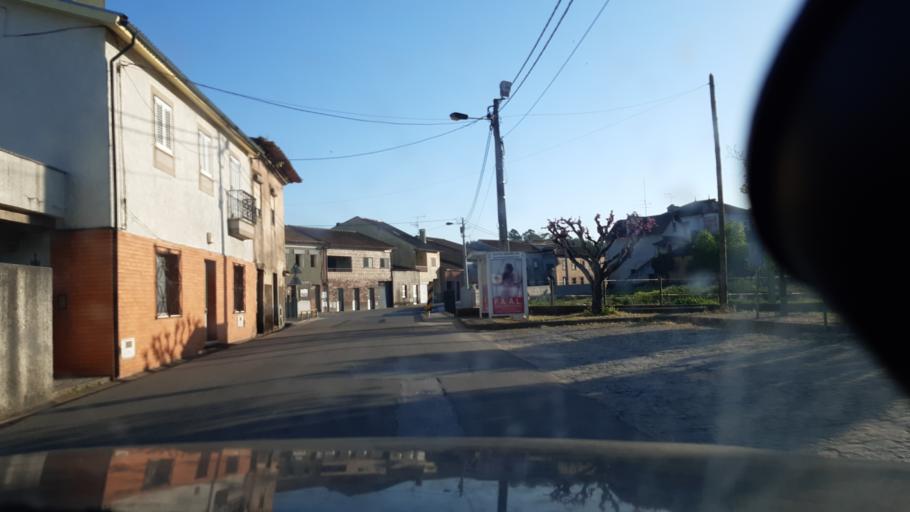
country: PT
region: Aveiro
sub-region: Agueda
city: Valongo
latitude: 40.6119
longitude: -8.4371
